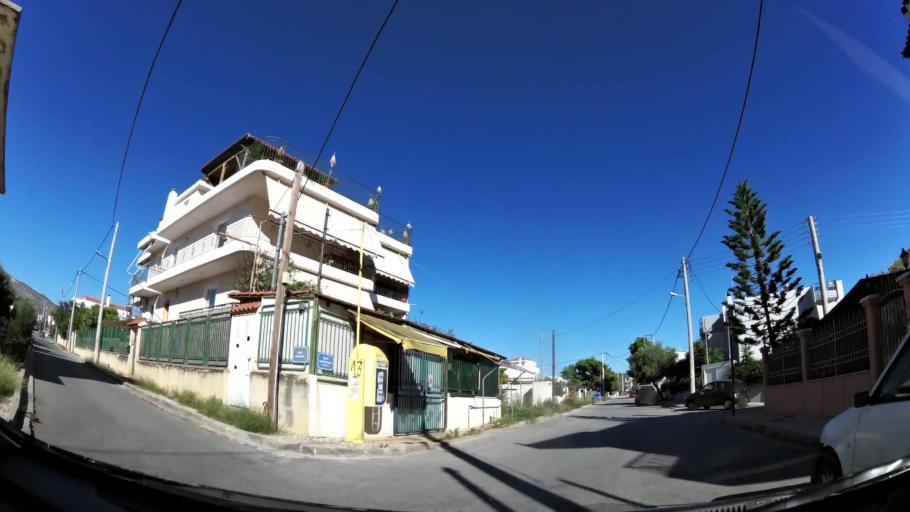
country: GR
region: Attica
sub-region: Nomarchia Anatolikis Attikis
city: Vari
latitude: 37.8361
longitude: 23.8104
